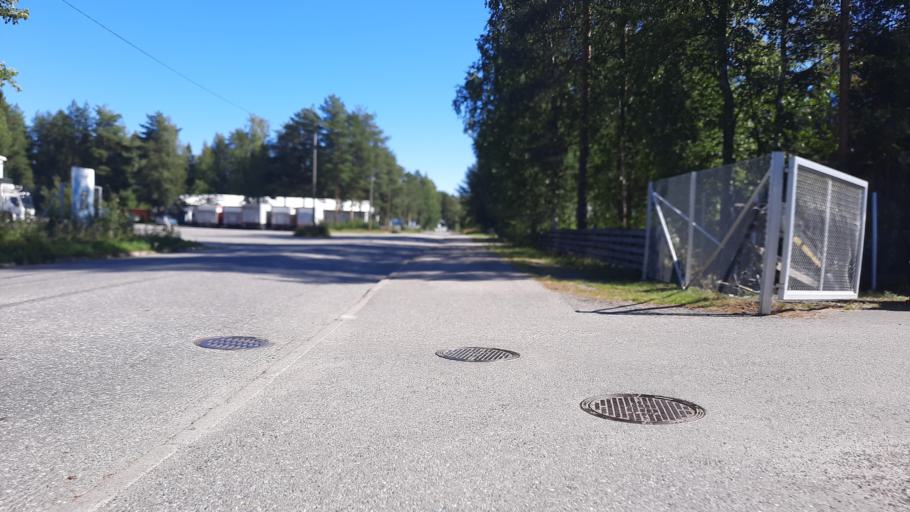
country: FI
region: North Karelia
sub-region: Joensuu
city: Joensuu
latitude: 62.6247
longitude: 29.7389
